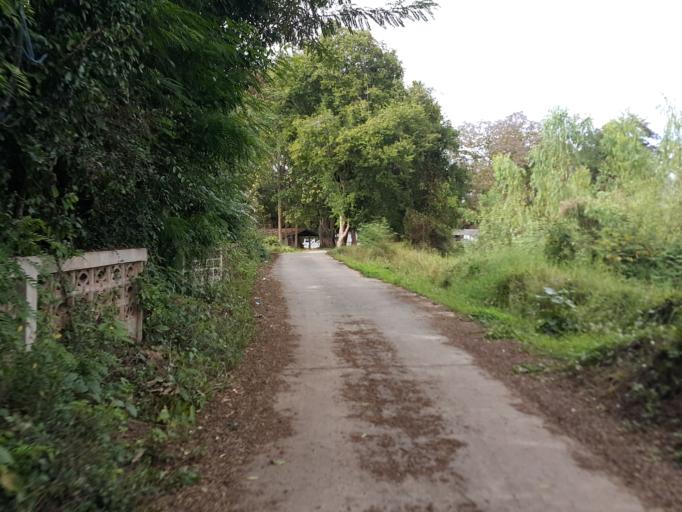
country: TH
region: Chiang Mai
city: San Sai
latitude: 18.8676
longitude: 99.0986
